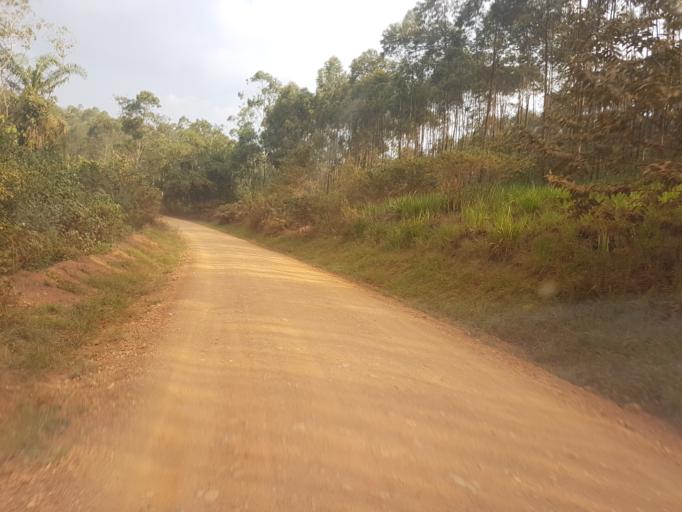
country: UG
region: Western Region
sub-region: Rukungiri District
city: Rukungiri
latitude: -0.6639
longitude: 29.8646
